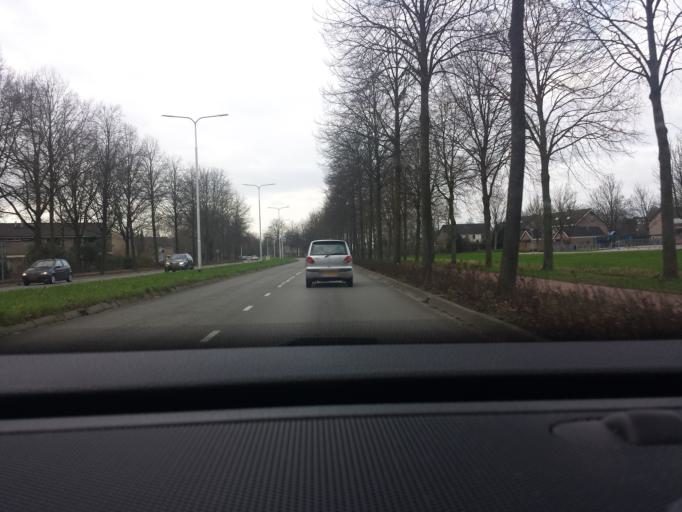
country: NL
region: Gelderland
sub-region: Gemeente Zevenaar
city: Zevenaar
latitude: 51.9381
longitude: 6.0717
